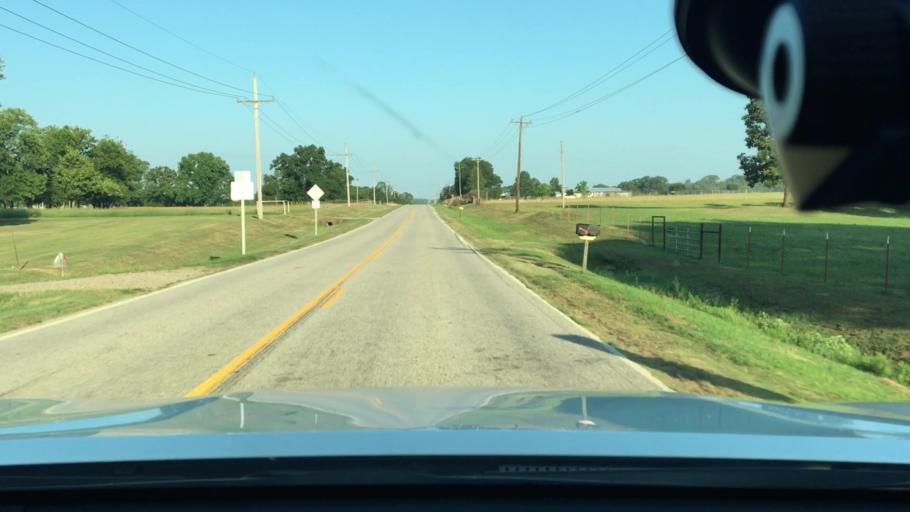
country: US
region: Arkansas
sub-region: Johnson County
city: Coal Hill
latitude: 35.3370
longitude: -93.6064
